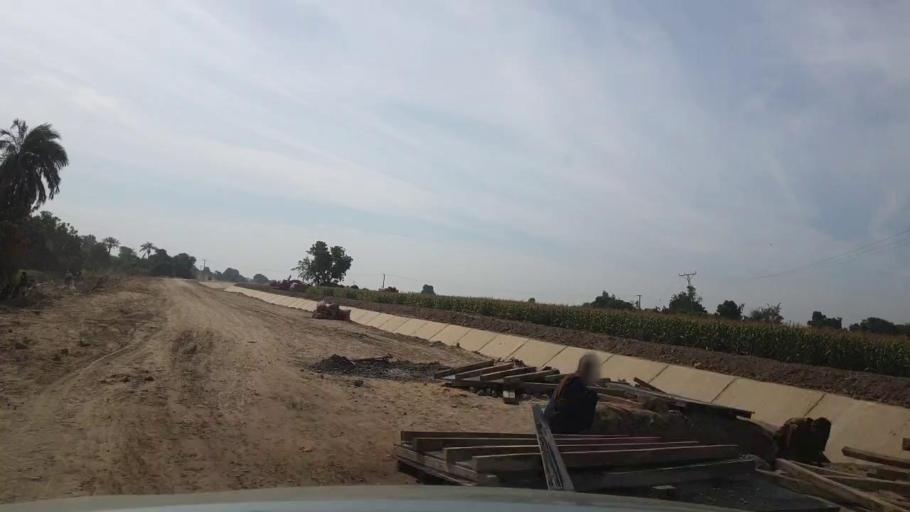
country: PK
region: Sindh
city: Kunri
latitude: 25.1612
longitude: 69.5891
